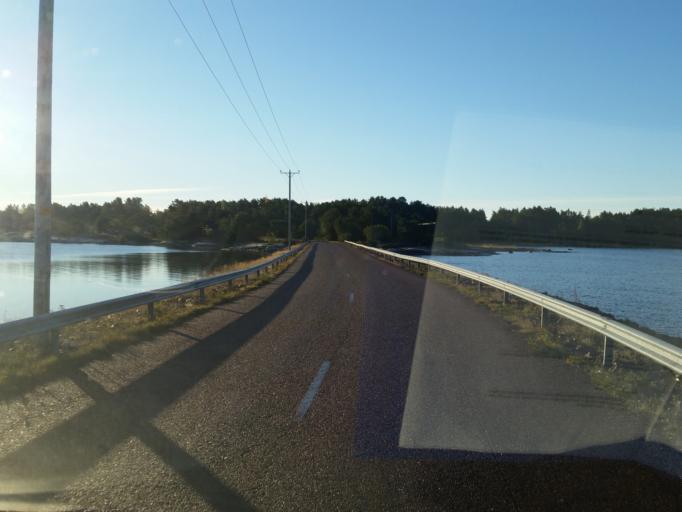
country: AX
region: Alands skaergard
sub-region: Vardoe
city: Vardoe
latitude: 60.3114
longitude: 20.3746
